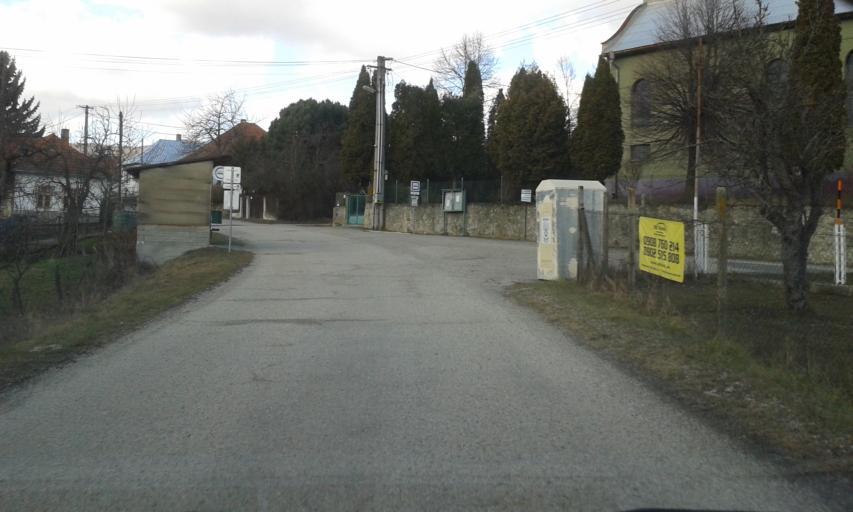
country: SK
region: Nitriansky
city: Zlate Moravce
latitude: 48.4626
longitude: 18.3153
